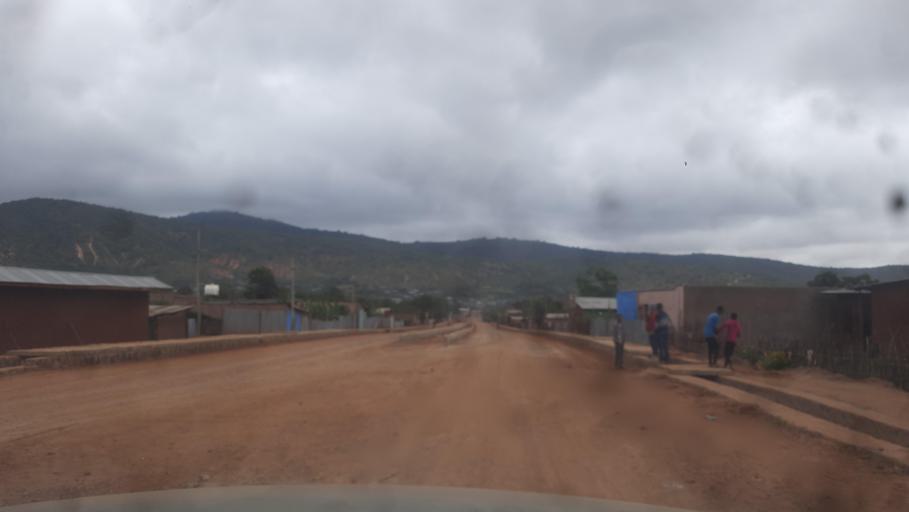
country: ET
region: Oromiya
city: Yabelo
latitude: 4.8959
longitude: 38.0855
